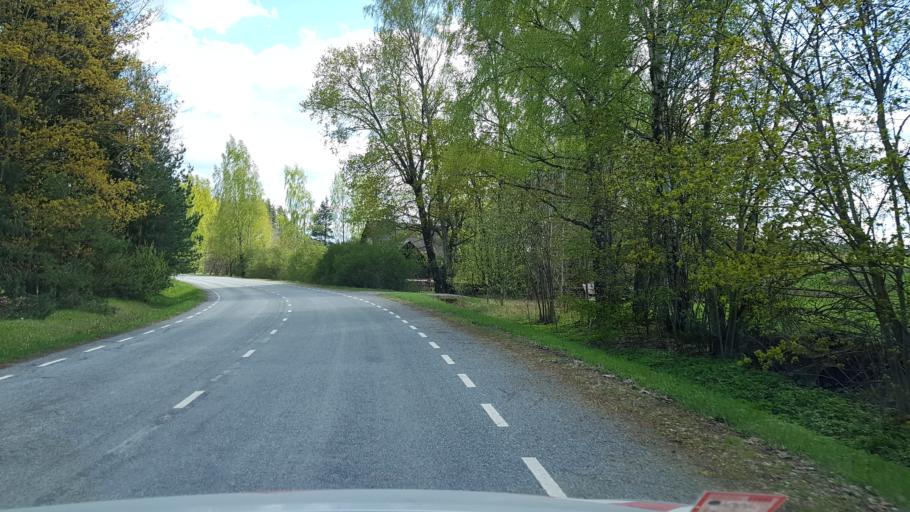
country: EE
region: Tartu
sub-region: UElenurme vald
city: Ulenurme
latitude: 58.2919
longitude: 26.8926
